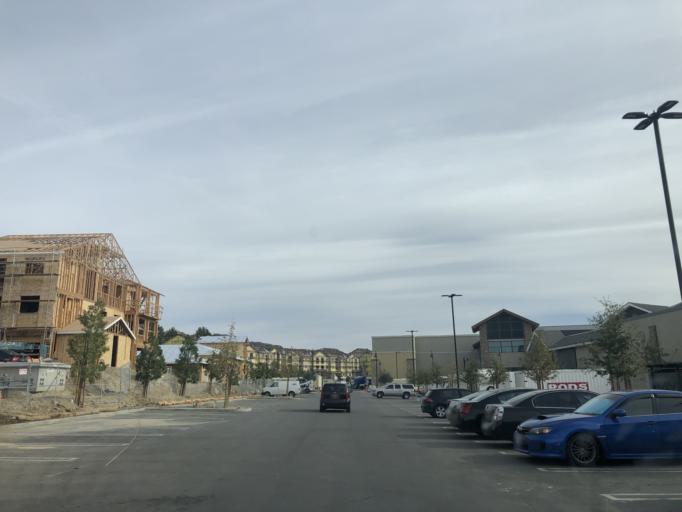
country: US
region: California
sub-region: Los Angeles County
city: Chatsworth
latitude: 34.2766
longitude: -118.5742
